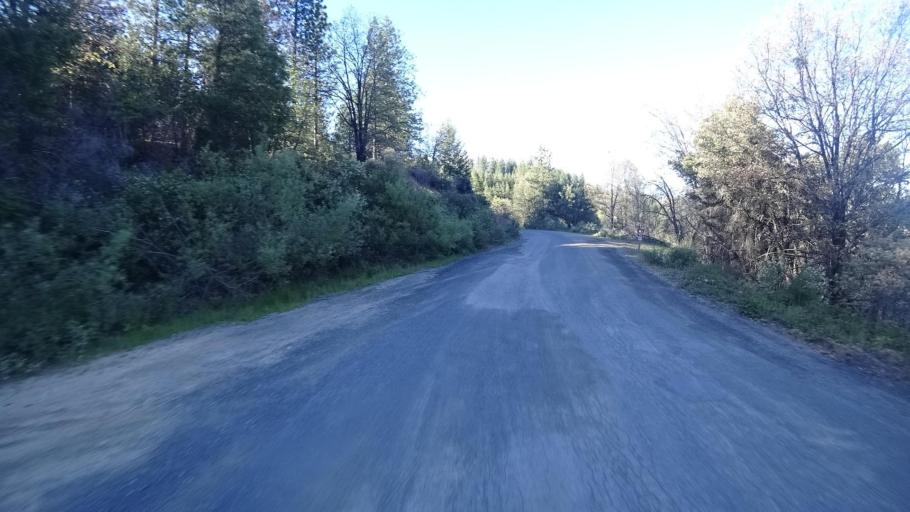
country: US
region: California
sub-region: Lake County
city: Upper Lake
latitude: 39.2920
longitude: -122.9244
